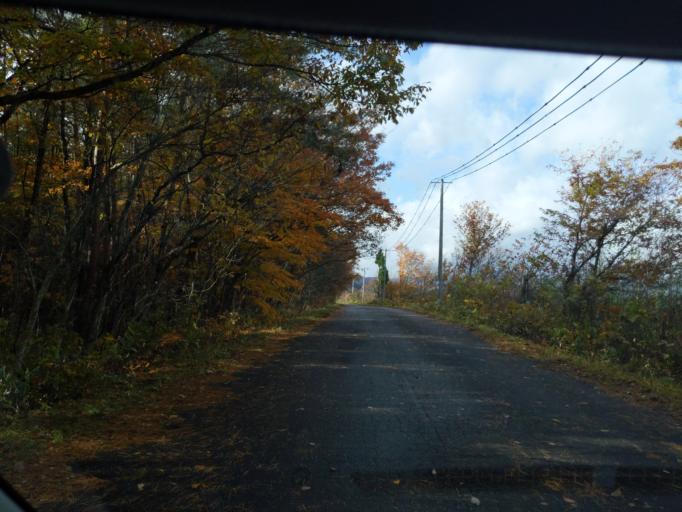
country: JP
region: Iwate
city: Mizusawa
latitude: 39.1040
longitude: 140.9751
